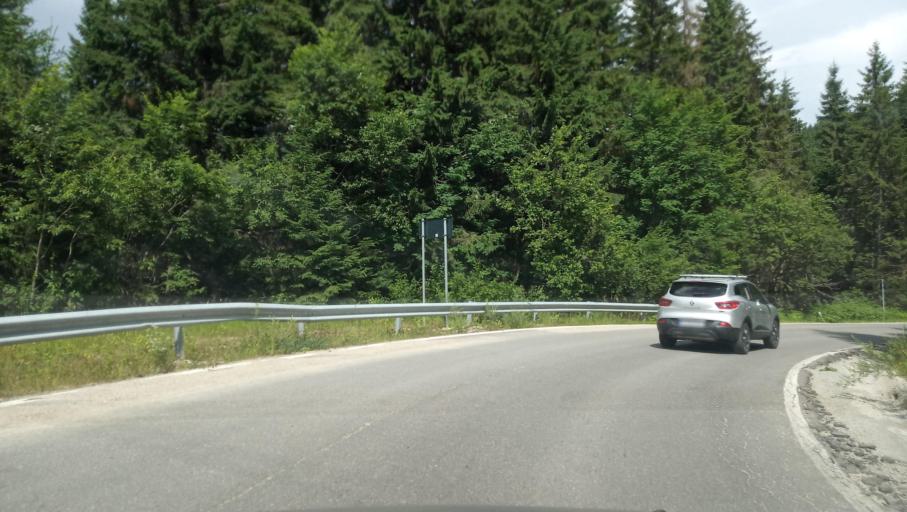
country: RO
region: Dambovita
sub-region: Comuna Moroeni
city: Glod
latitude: 45.3271
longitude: 25.4366
